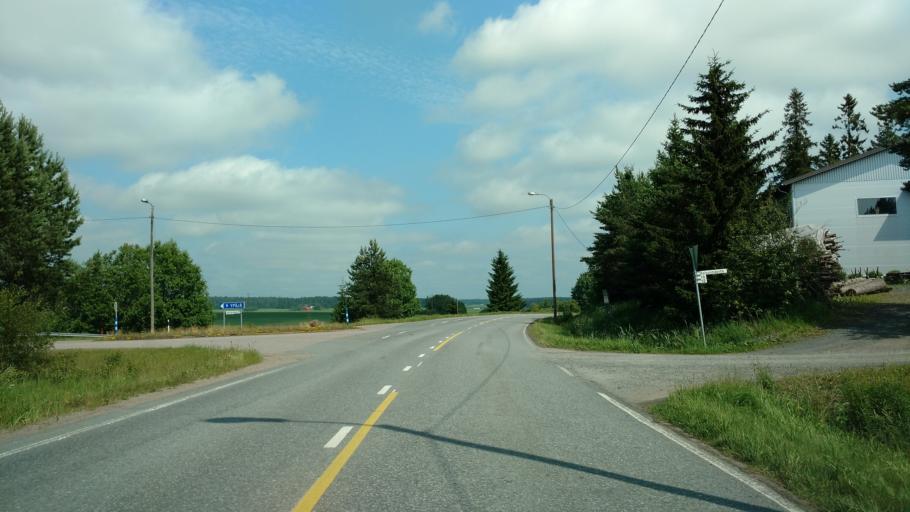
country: FI
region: Haeme
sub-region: Forssa
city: Jokioinen
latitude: 60.7898
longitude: 23.4182
